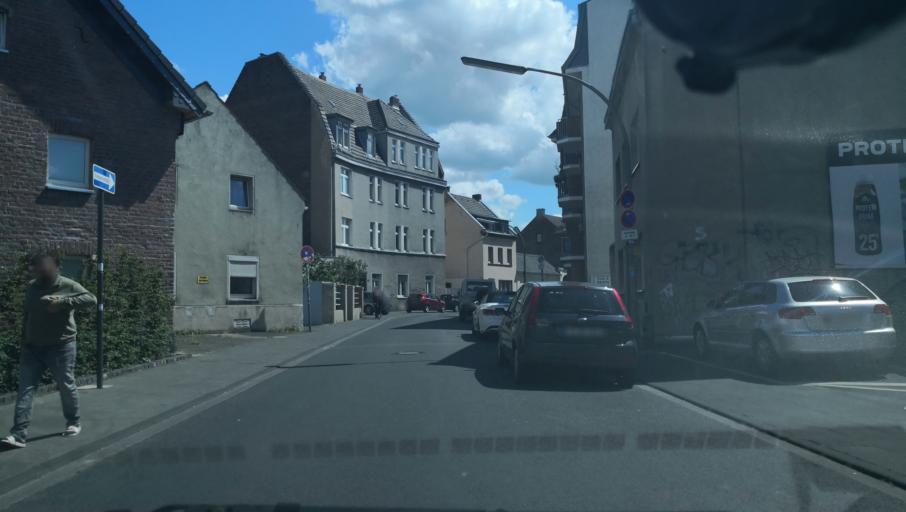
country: DE
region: North Rhine-Westphalia
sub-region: Regierungsbezirk Koln
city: Bilderstoeckchen
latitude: 50.9595
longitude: 6.9015
